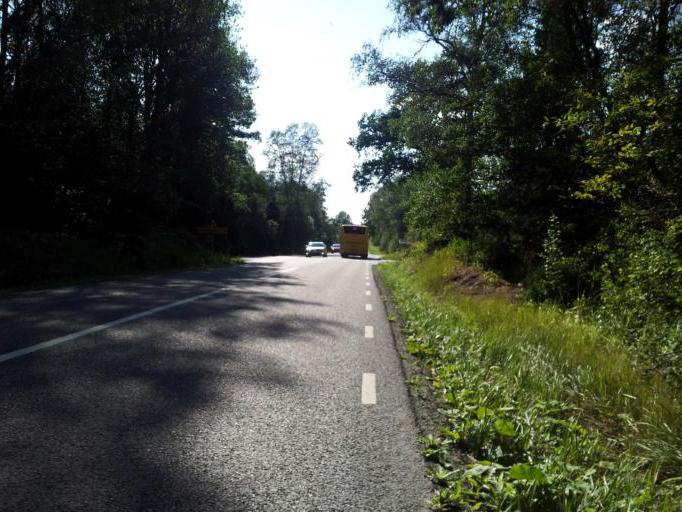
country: SE
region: Uppsala
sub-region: Knivsta Kommun
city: Knivsta
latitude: 59.8610
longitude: 17.9272
